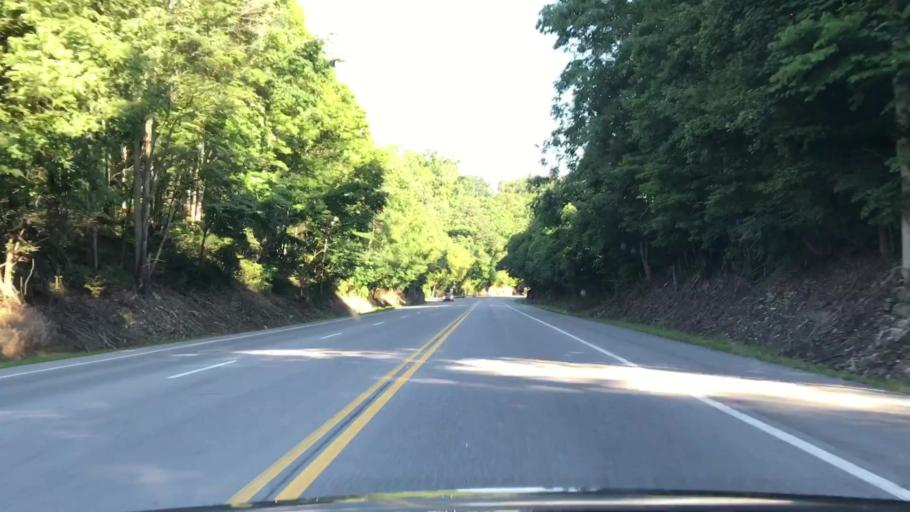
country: US
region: Tennessee
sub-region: Jackson County
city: Gainesboro
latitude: 36.3058
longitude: -85.6427
